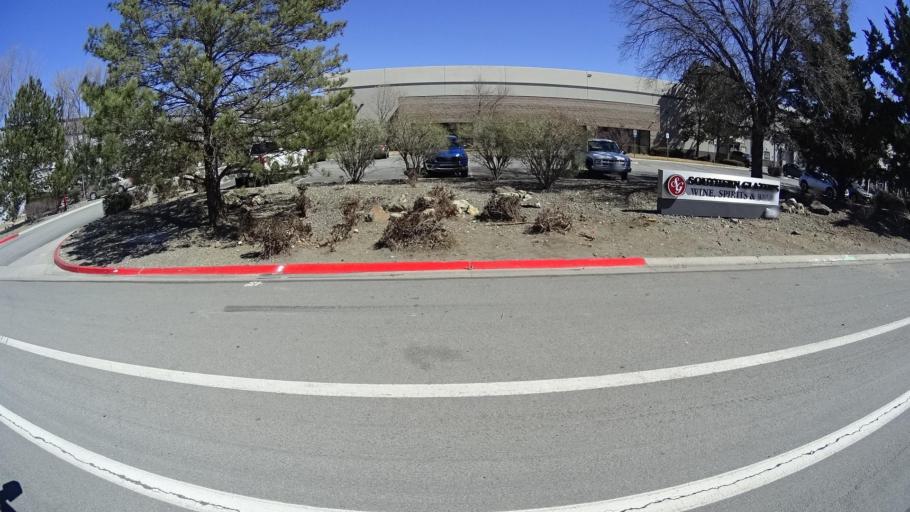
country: US
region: Nevada
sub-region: Washoe County
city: Sparks
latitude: 39.5315
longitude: -119.7112
